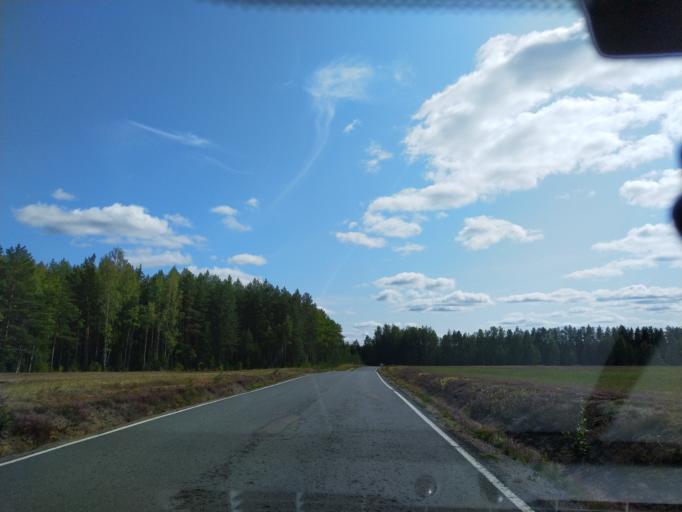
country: FI
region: Uusimaa
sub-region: Helsinki
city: Kaerkoelae
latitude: 60.7427
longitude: 24.1224
